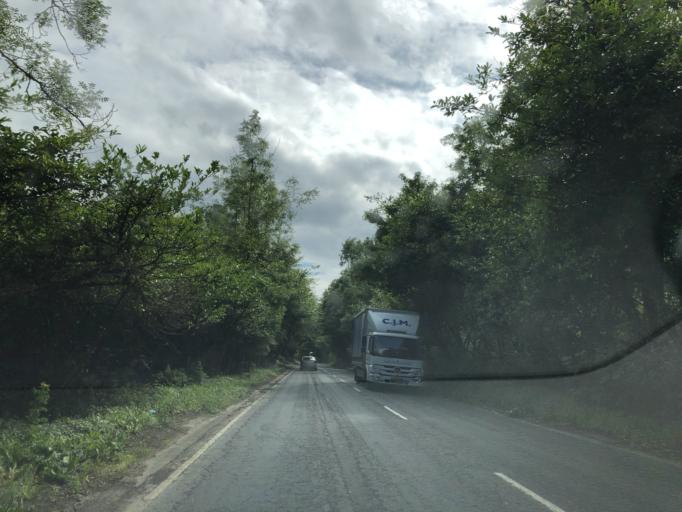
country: GB
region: Northern Ireland
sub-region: Down District
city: Dundrum
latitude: 54.3117
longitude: -5.8410
